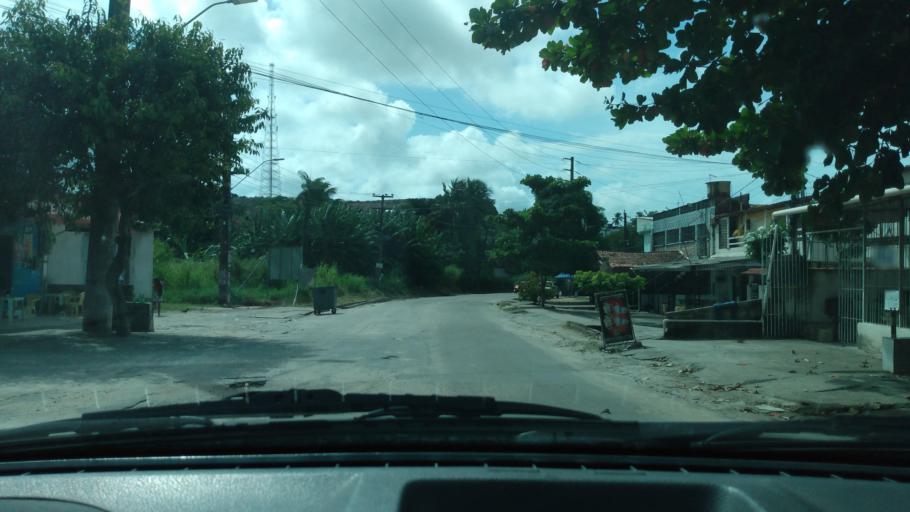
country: BR
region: Pernambuco
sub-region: Cabo De Santo Agostinho
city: Cabo
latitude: -8.3407
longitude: -34.9558
